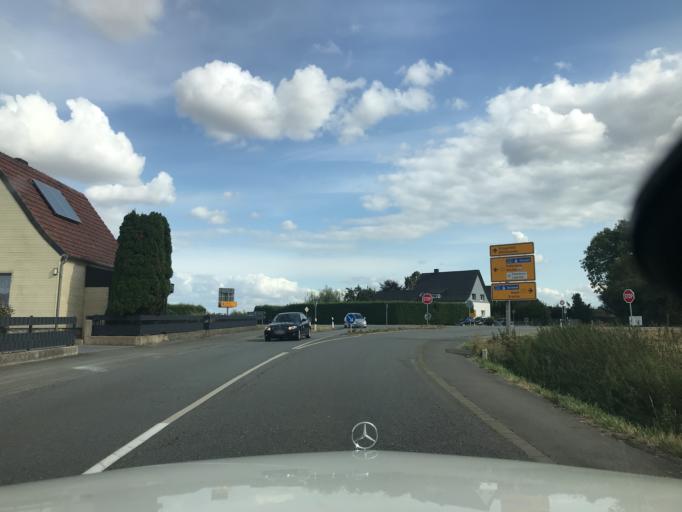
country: DE
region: North Rhine-Westphalia
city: Geseke
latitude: 51.6272
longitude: 8.4254
